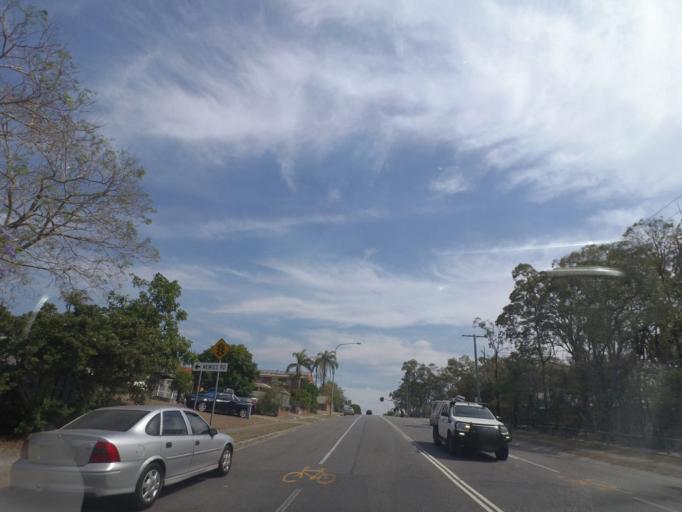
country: AU
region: Queensland
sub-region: Brisbane
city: Sunnybank Hills
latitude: -27.6024
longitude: 153.0637
